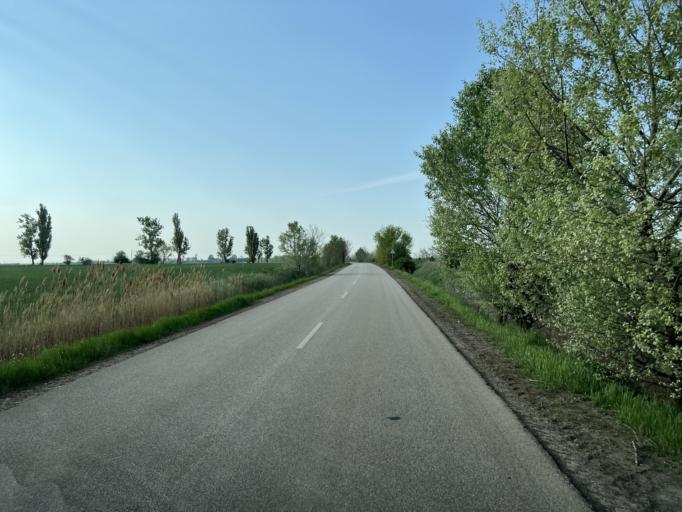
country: HU
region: Pest
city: Abony
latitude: 47.1170
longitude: 20.0142
